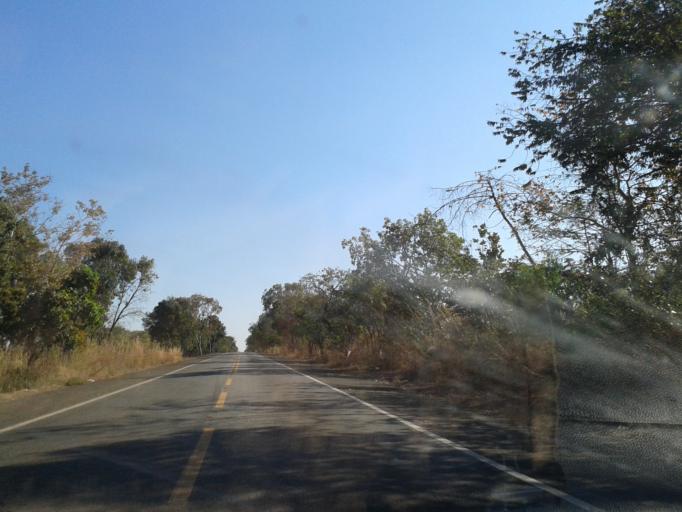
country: BR
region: Goias
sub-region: Mozarlandia
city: Mozarlandia
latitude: -14.8159
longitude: -50.5316
